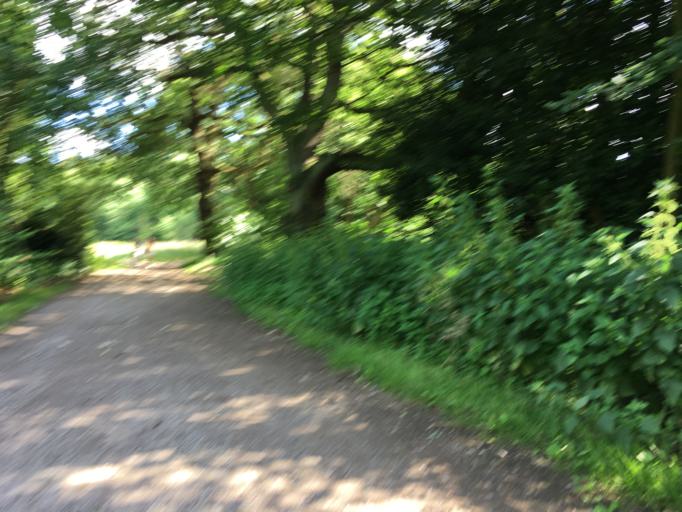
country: GB
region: England
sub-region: Greater London
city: Belsize Park
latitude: 51.5711
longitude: -0.1813
